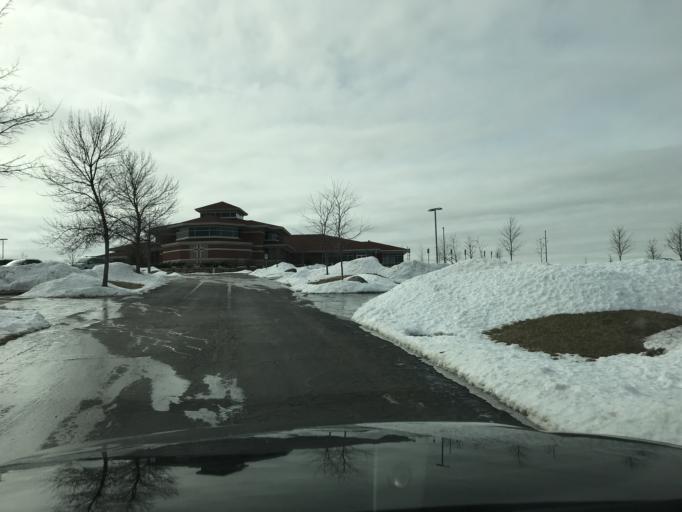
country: US
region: Wisconsin
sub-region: Dane County
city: Cottage Grove
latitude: 43.0931
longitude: -89.2642
